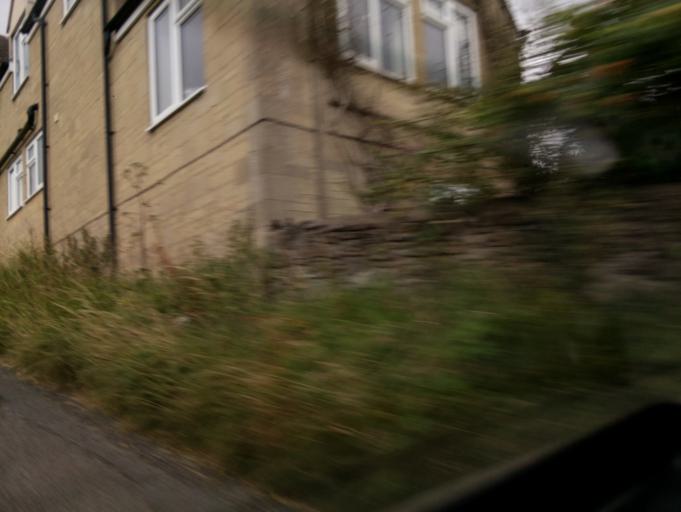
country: GB
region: England
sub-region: Gloucestershire
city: Painswick
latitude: 51.8154
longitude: -2.1498
